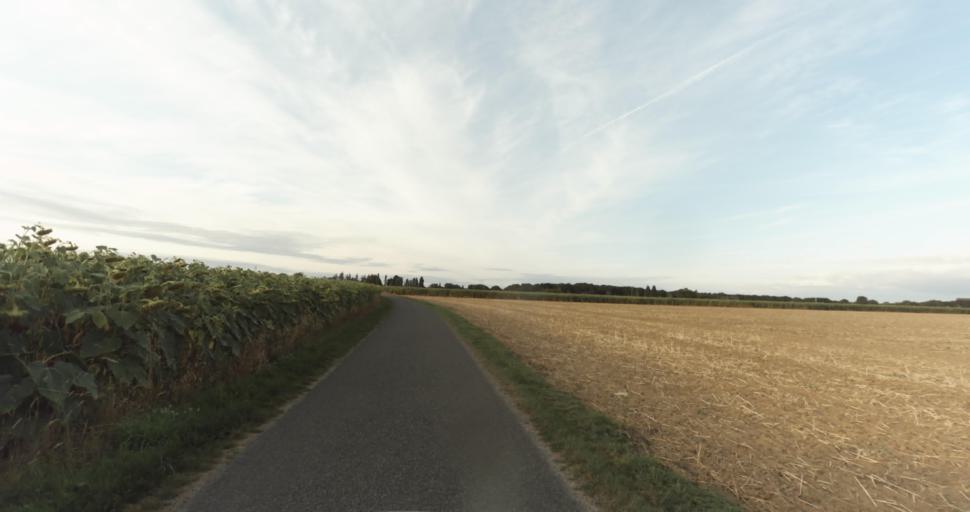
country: FR
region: Haute-Normandie
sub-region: Departement de l'Eure
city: Marcilly-sur-Eure
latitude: 48.8420
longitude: 1.2722
